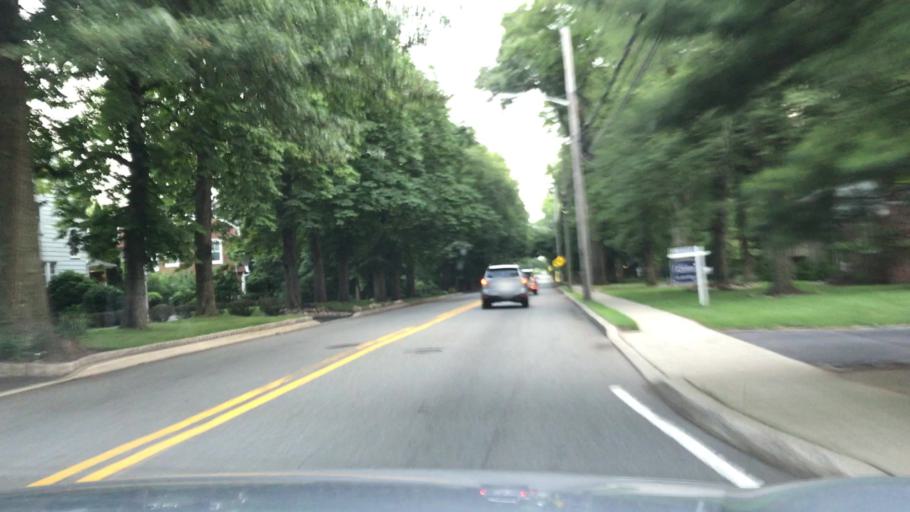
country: US
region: New Jersey
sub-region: Bergen County
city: Haworth
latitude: 40.9599
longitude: -73.9838
